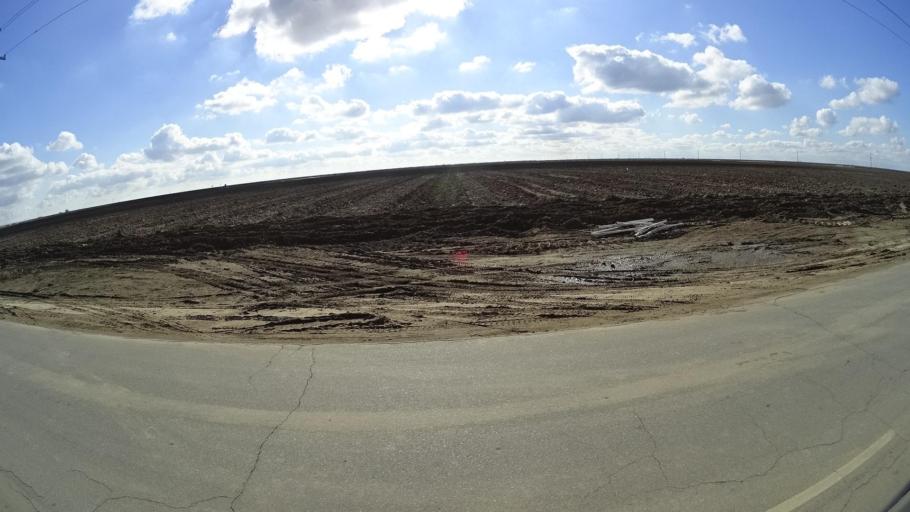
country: US
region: California
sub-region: Kern County
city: McFarland
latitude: 35.6743
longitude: -119.2729
